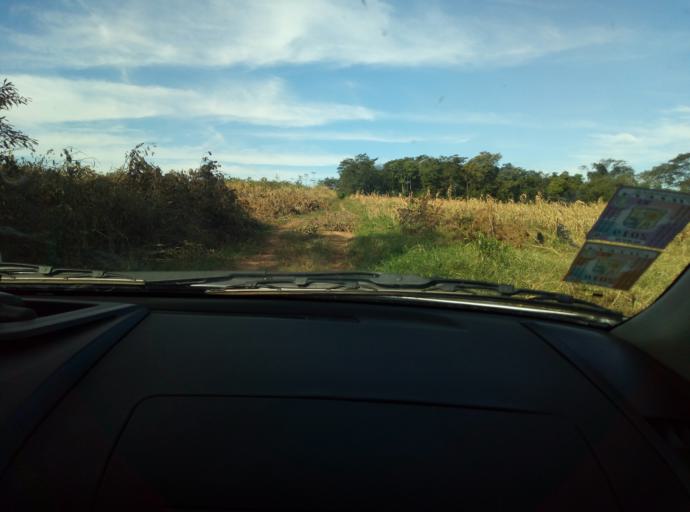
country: PY
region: Caaguazu
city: Carayao
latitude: -25.1727
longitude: -56.2833
